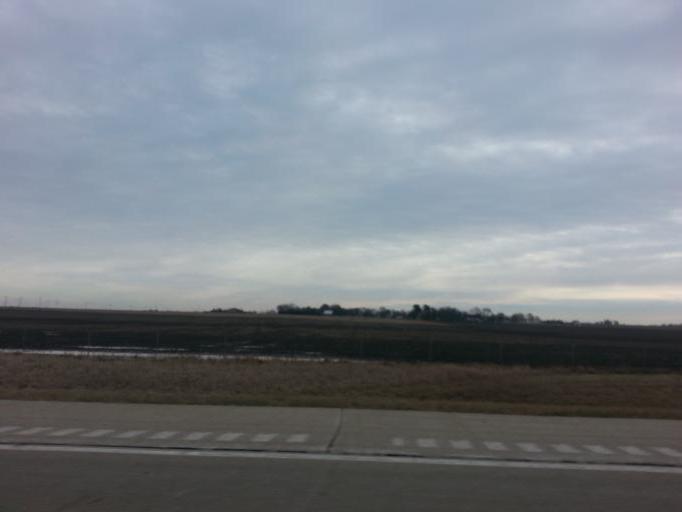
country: US
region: Illinois
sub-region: Woodford County
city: El Paso
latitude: 40.7845
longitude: -89.0349
